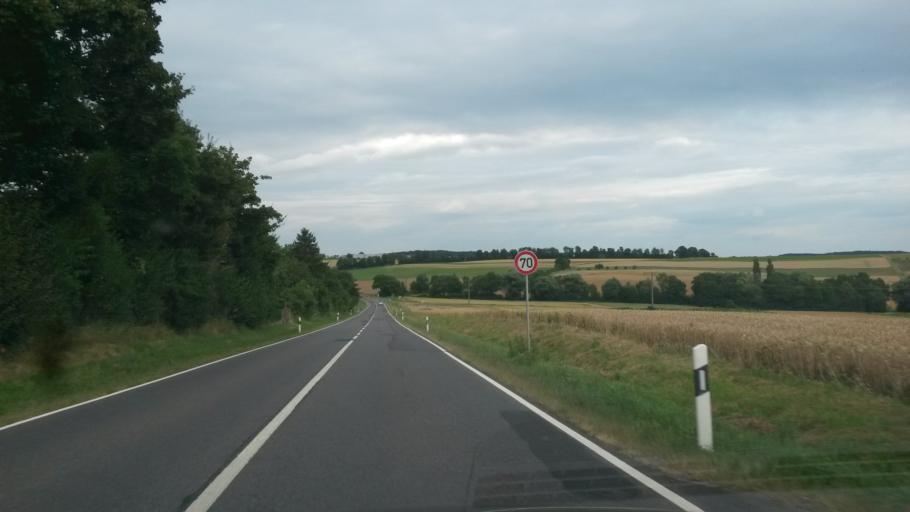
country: DE
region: Bavaria
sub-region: Regierungsbezirk Unterfranken
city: Hettstadt
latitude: 49.7986
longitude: 9.8121
